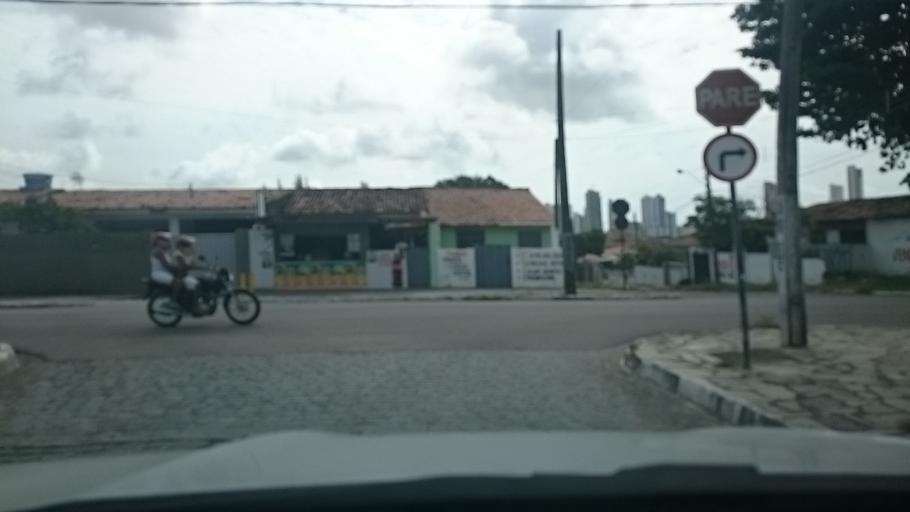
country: BR
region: Paraiba
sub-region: Joao Pessoa
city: Joao Pessoa
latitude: -7.1308
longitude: -34.8403
